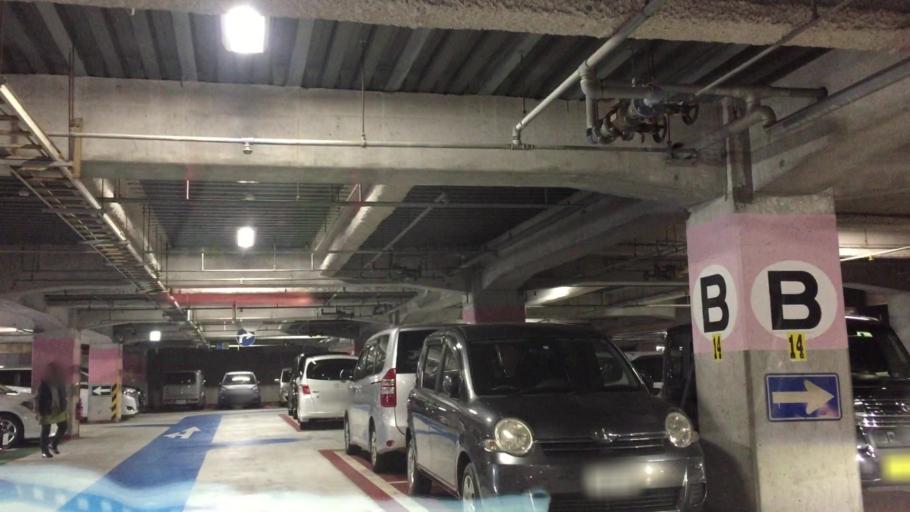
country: JP
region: Kanagawa
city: Zushi
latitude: 35.3332
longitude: 139.6209
